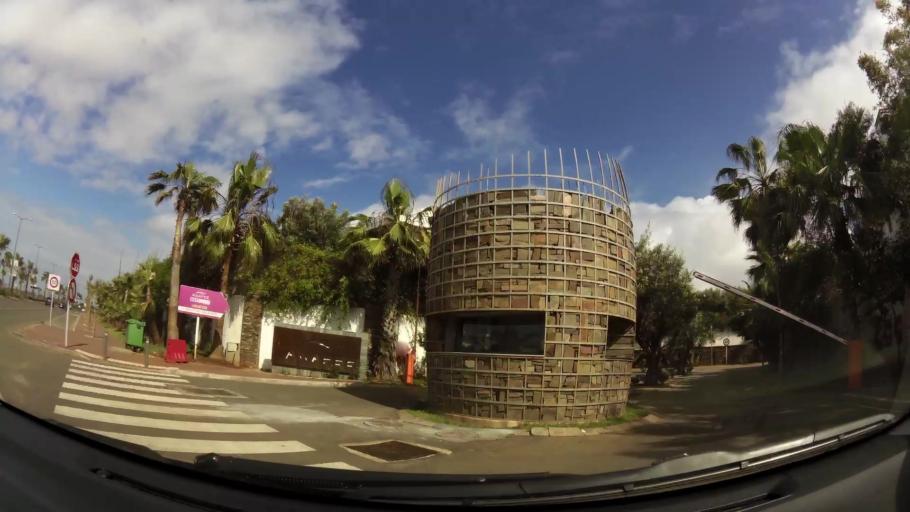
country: MA
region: Grand Casablanca
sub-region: Casablanca
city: Casablanca
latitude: 33.5692
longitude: -7.7061
